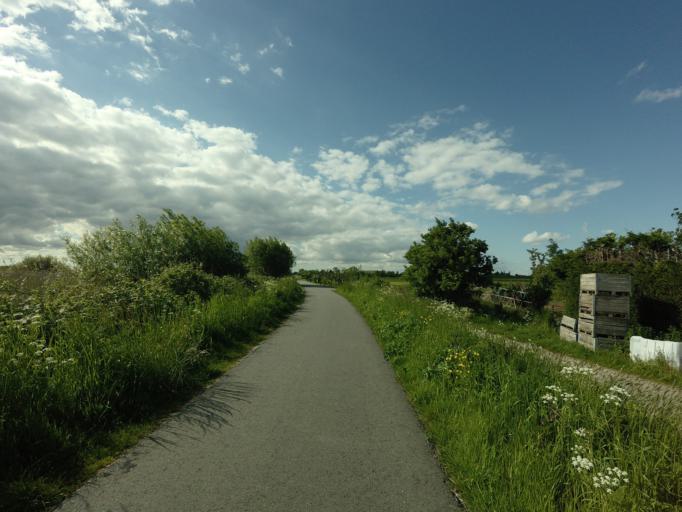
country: NL
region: Utrecht
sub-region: Gemeente Lopik
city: Lopik
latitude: 51.9565
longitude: 4.9901
